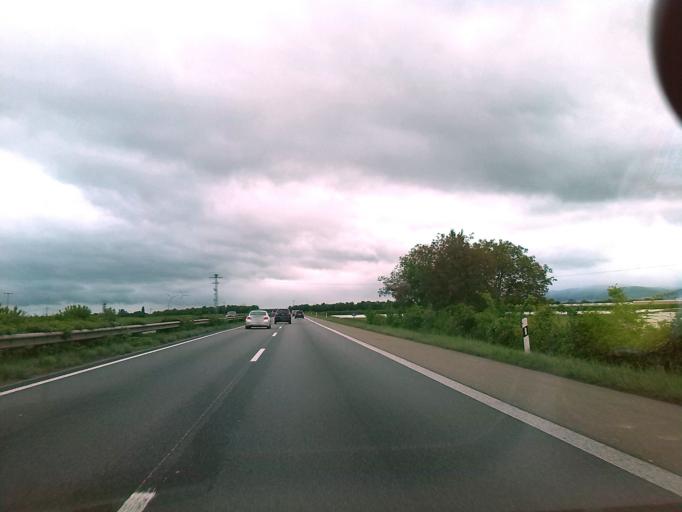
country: DE
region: Rheinland-Pfalz
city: Hochdorf-Assenheim
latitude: 49.4159
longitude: 8.2879
